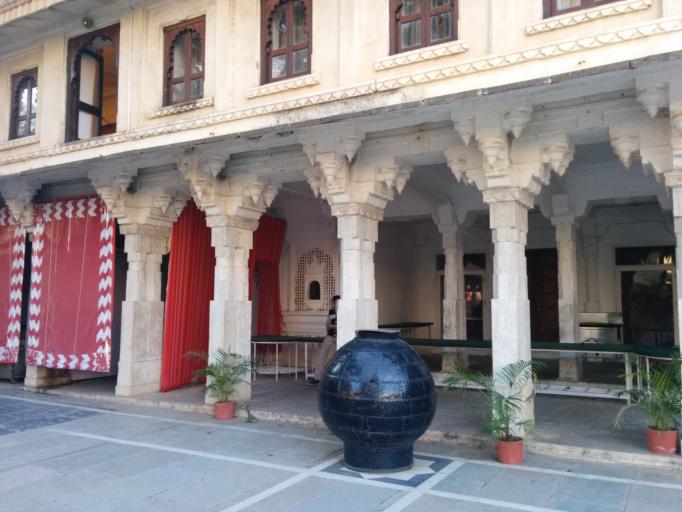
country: IN
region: Rajasthan
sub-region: Udaipur
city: Udaipur
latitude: 24.5759
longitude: 73.6833
